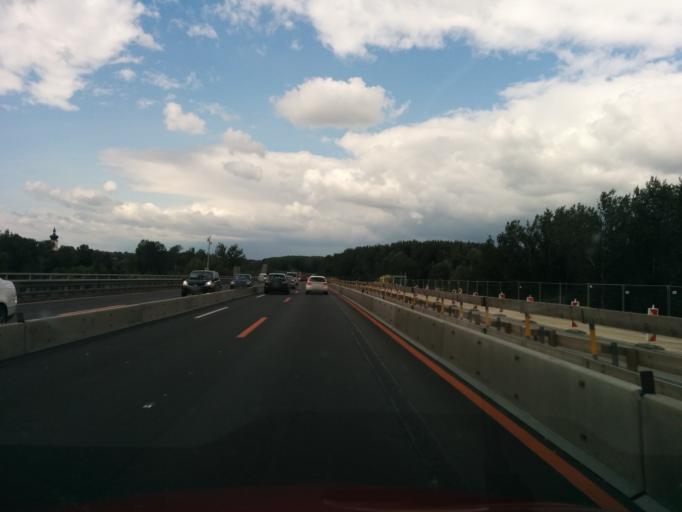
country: AT
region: Lower Austria
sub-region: Politischer Bezirk Wien-Umgebung
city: Fischamend Dorf
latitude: 48.1193
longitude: 16.6233
